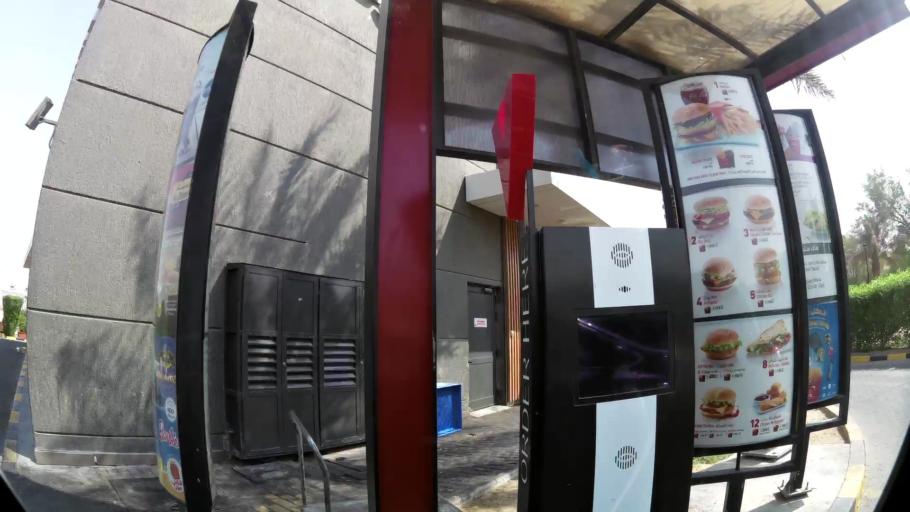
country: KW
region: Muhafazat al Jahra'
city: Al Jahra'
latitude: 29.3395
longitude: 47.6876
